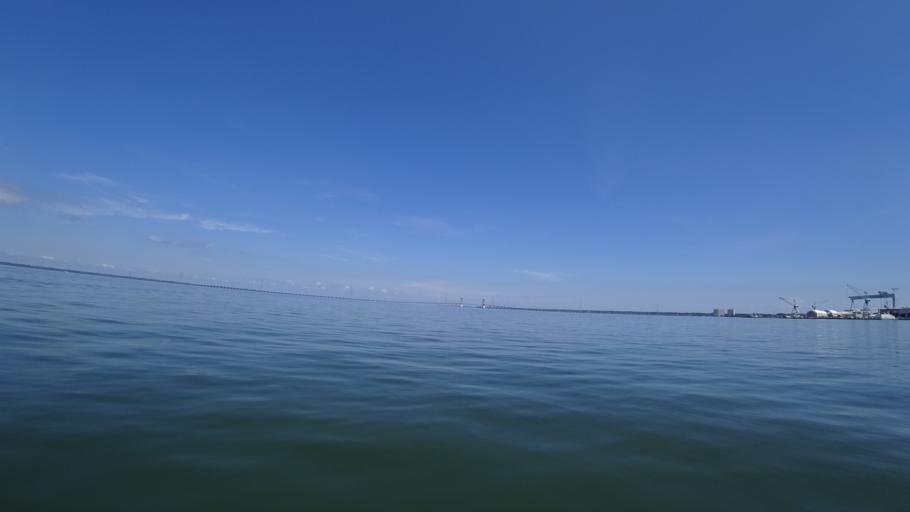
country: US
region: Virginia
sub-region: City of Newport News
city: Newport News
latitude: 36.9867
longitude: -76.4531
